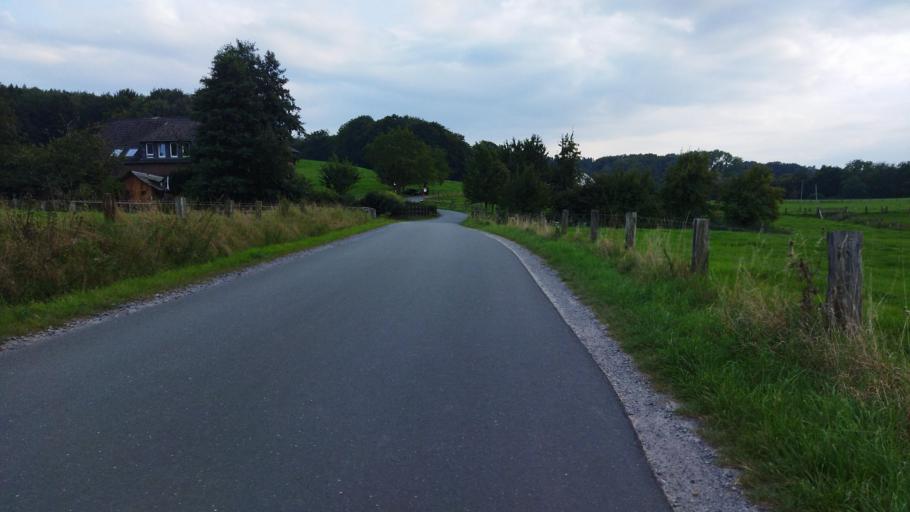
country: DE
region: Lower Saxony
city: Hagen
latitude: 52.1841
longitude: 8.0077
